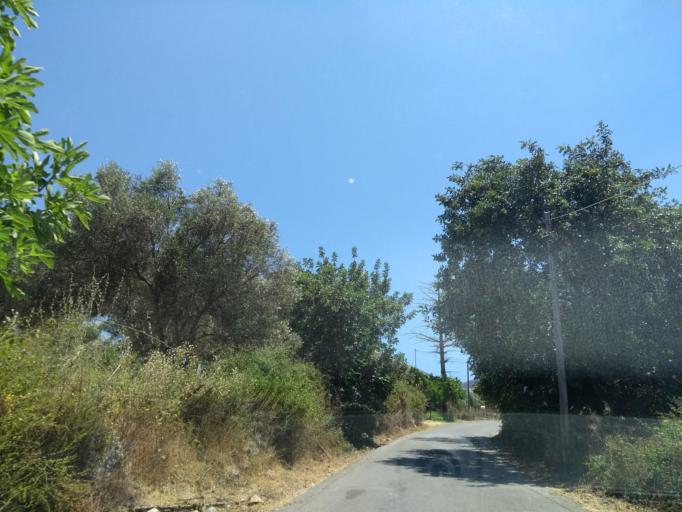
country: GR
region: Crete
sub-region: Nomos Chanias
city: Georgioupolis
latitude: 35.3190
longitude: 24.3096
